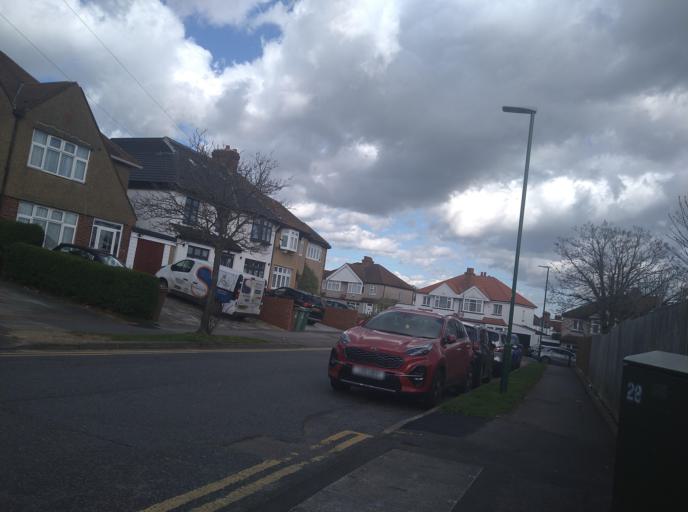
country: GB
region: England
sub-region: Greater London
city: Carshalton
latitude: 51.3747
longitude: -0.1830
